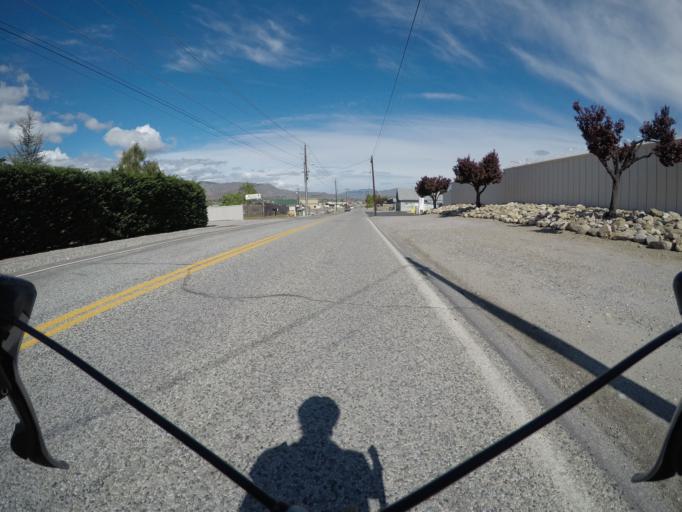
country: US
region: Washington
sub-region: Chelan County
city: South Wenatchee
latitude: 47.3978
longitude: -120.2831
